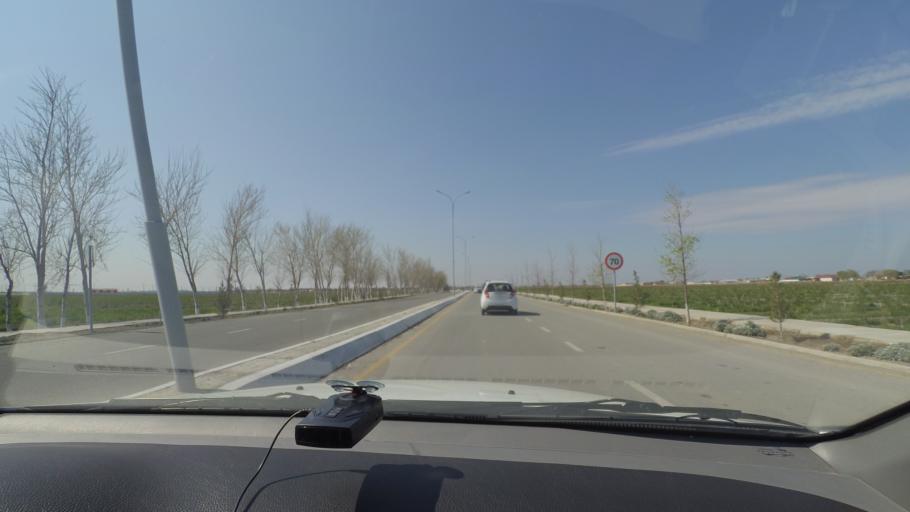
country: UZ
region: Bukhara
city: Bukhara
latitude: 39.8011
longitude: 64.4885
